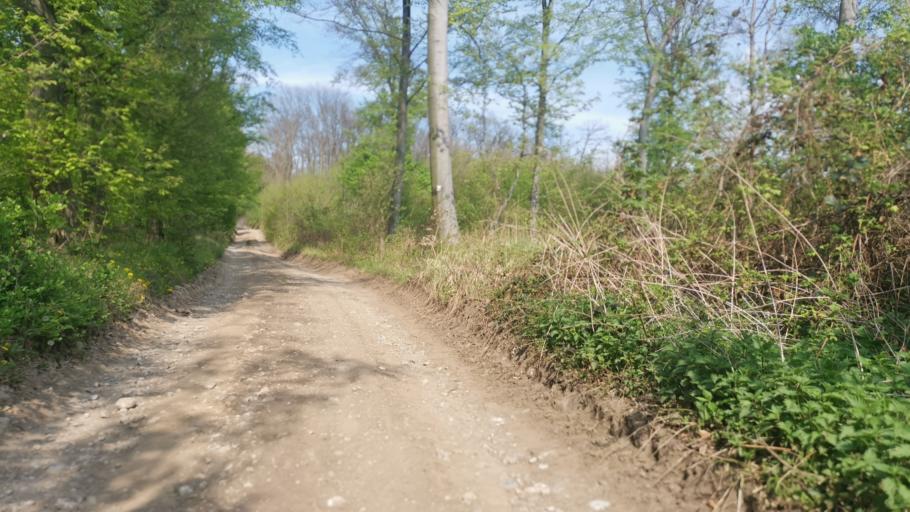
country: SK
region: Trnavsky
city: Smolenice
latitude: 48.5705
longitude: 17.3665
